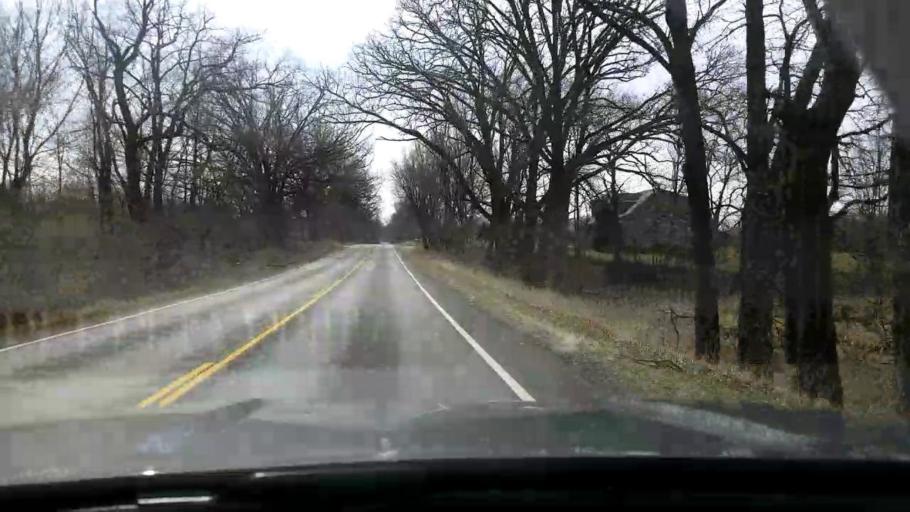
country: US
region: Michigan
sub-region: Jackson County
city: Spring Arbor
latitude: 42.1839
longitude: -84.5204
